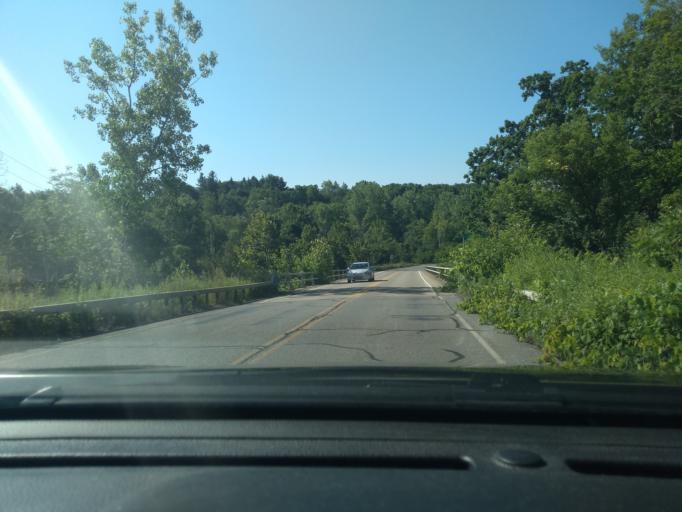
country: US
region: New York
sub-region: Erie County
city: Billington Heights
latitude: 42.7801
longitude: -78.6832
